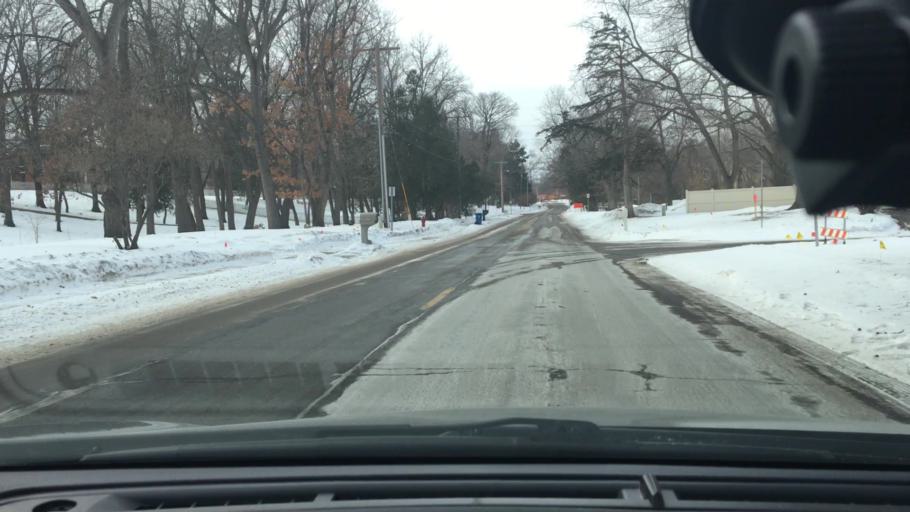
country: US
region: Minnesota
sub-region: Hennepin County
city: Champlin
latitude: 45.1861
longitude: -93.3950
